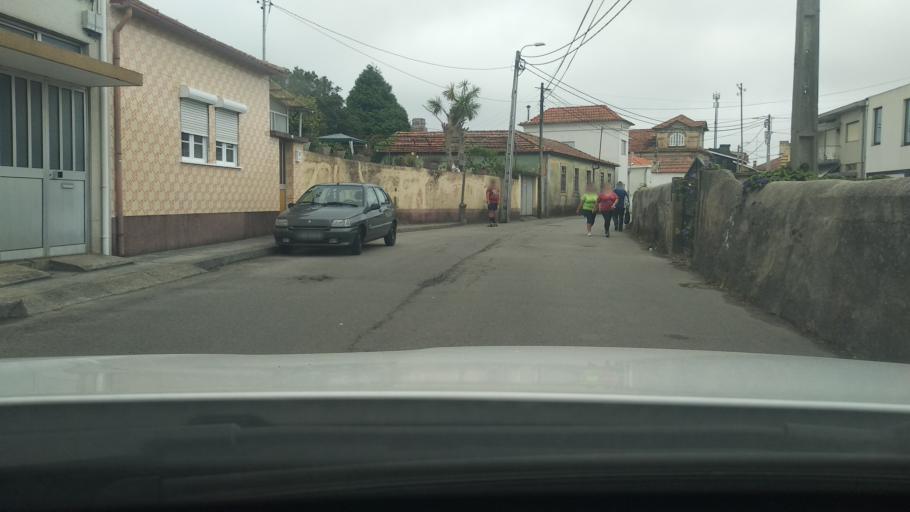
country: PT
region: Aveiro
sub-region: Espinho
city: Silvalde
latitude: 40.9911
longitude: -8.6255
